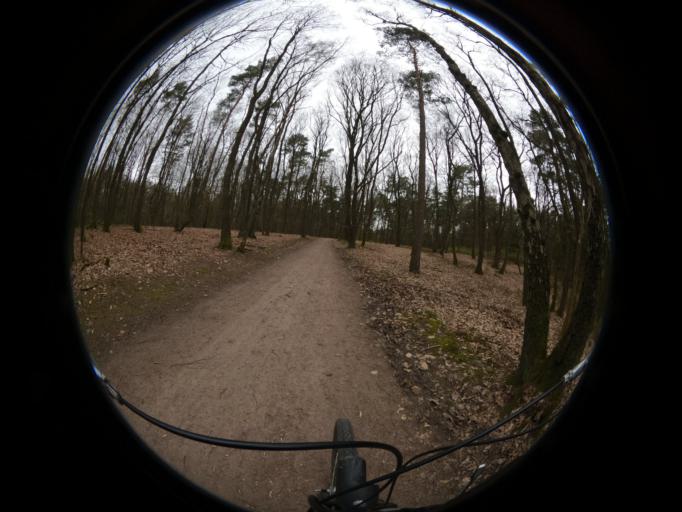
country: DE
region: Lower Saxony
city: Neu Wulmstorf
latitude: 53.4481
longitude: 9.8521
